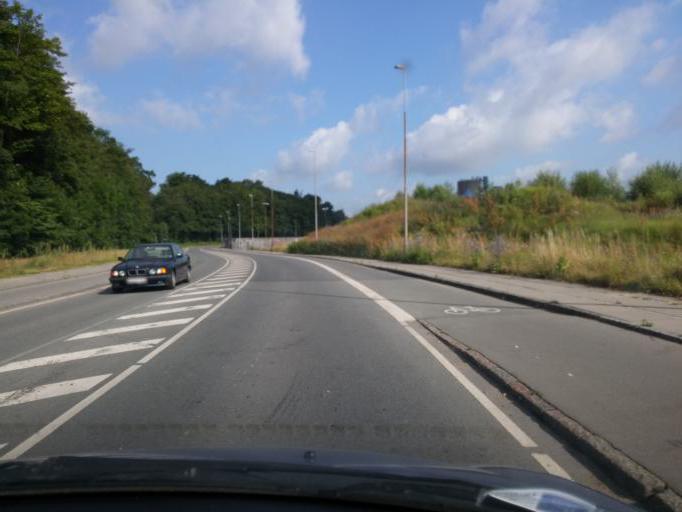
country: DK
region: South Denmark
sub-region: Odense Kommune
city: Odense
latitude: 55.4059
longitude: 10.3775
